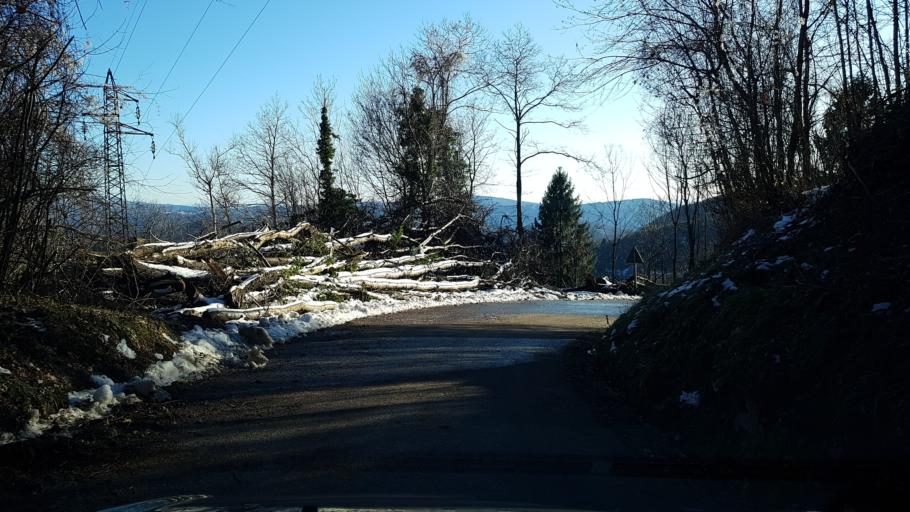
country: IT
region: Friuli Venezia Giulia
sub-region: Provincia di Udine
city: Savogna
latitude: 46.1896
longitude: 13.5290
